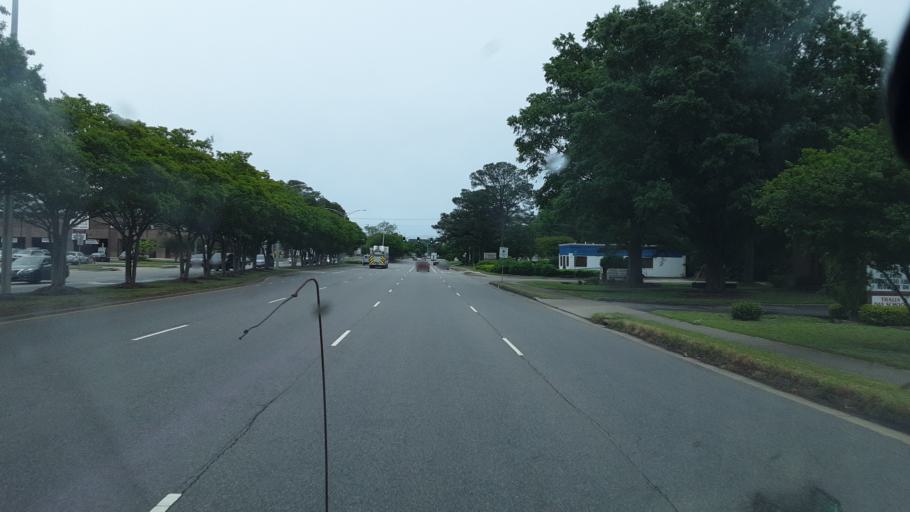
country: US
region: Virginia
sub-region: City of Virginia Beach
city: Virginia Beach
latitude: 36.8433
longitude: -76.1231
